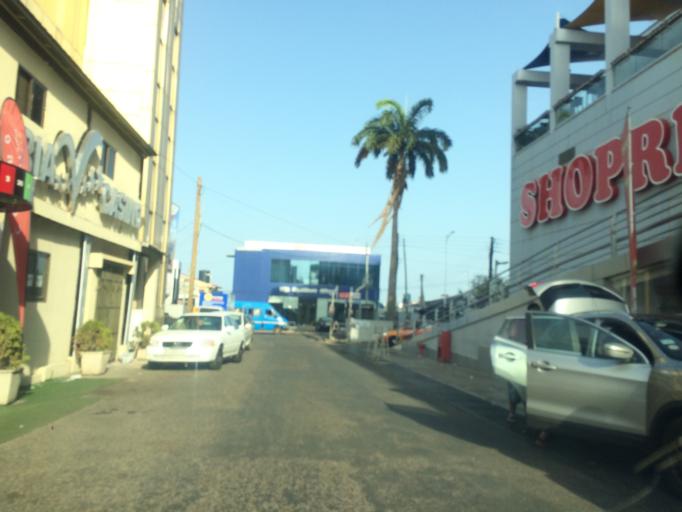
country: GH
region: Greater Accra
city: Accra
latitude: 5.5608
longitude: -0.1825
